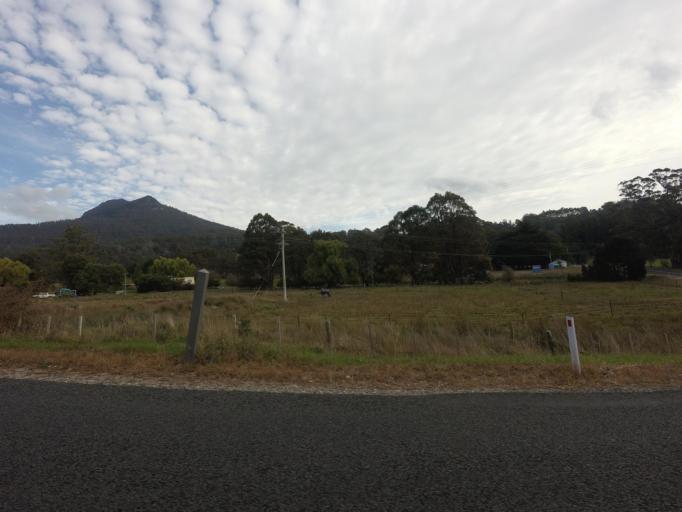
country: AU
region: Tasmania
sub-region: Meander Valley
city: Deloraine
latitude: -41.6287
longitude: 146.7105
